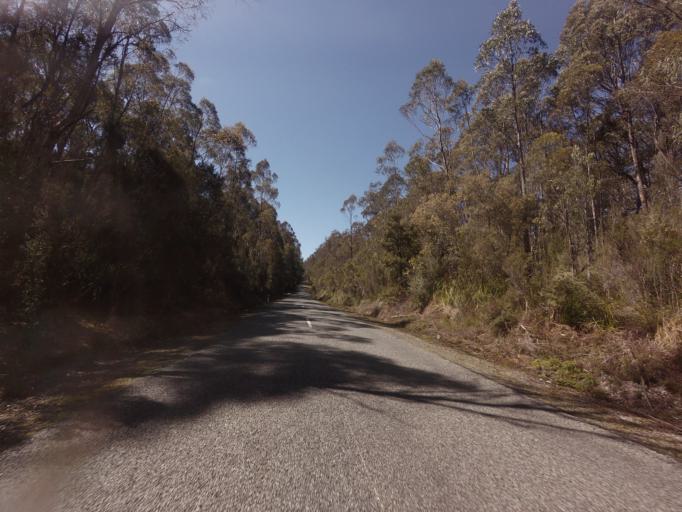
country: AU
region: Tasmania
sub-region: Derwent Valley
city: New Norfolk
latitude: -42.7524
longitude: 146.4111
